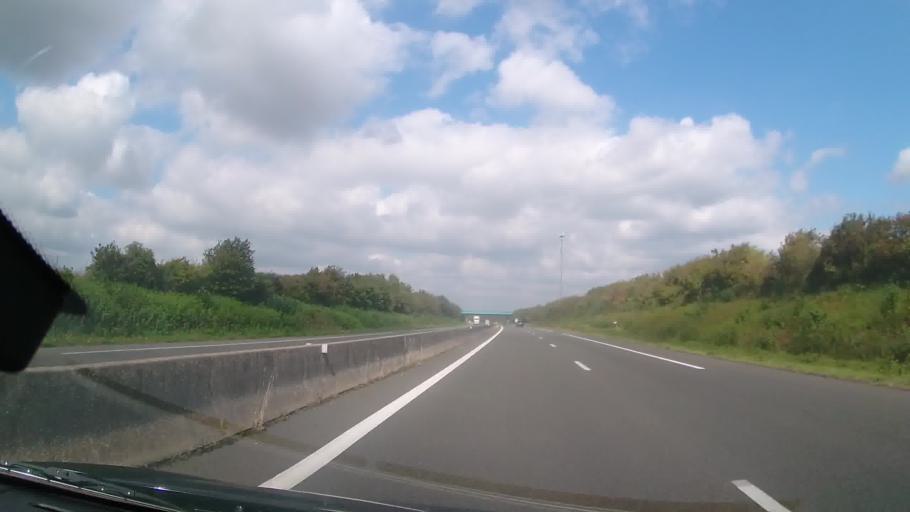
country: FR
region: Picardie
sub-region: Departement de la Somme
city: Sailly-Flibeaucourt
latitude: 50.2009
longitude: 1.7590
